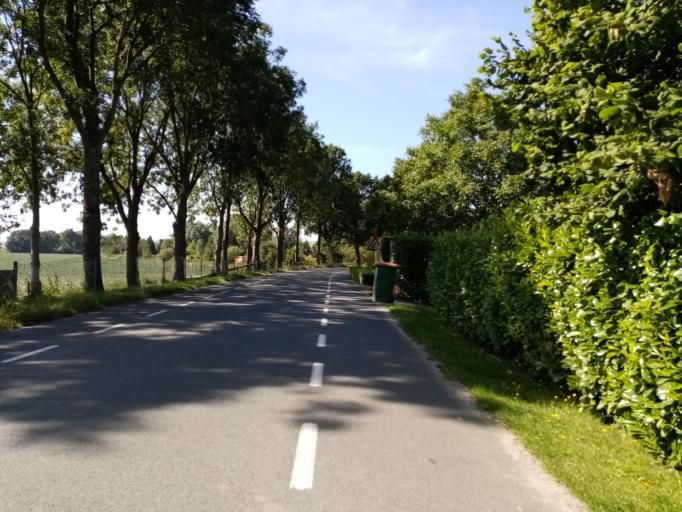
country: NL
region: North Brabant
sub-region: Gemeente Moerdijk
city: Klundert
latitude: 51.6523
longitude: 4.6159
